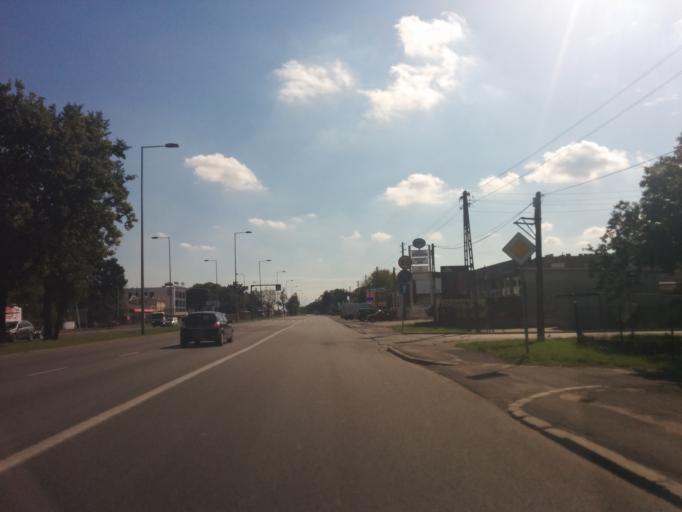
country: PL
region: Masovian Voivodeship
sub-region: Warszawa
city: Bialoleka
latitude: 52.3284
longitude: 20.9672
